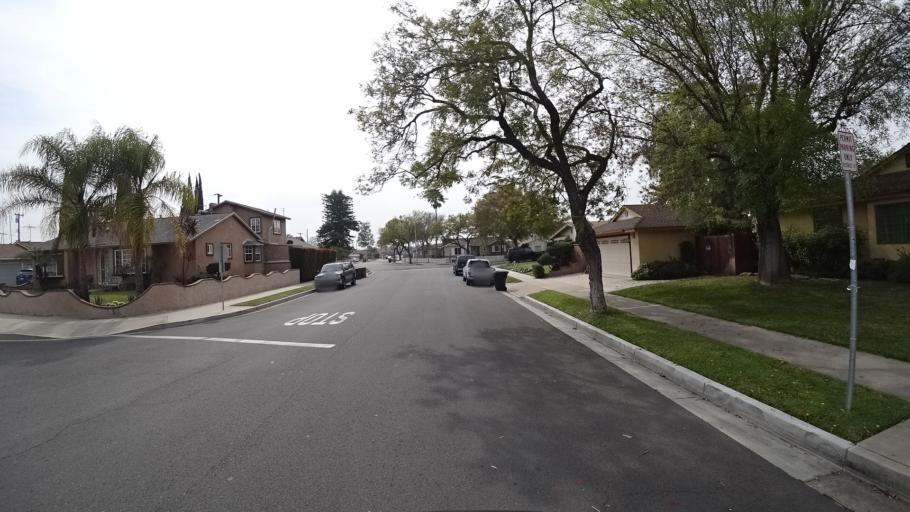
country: US
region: California
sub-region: Orange County
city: Anaheim
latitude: 33.8217
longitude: -117.9459
